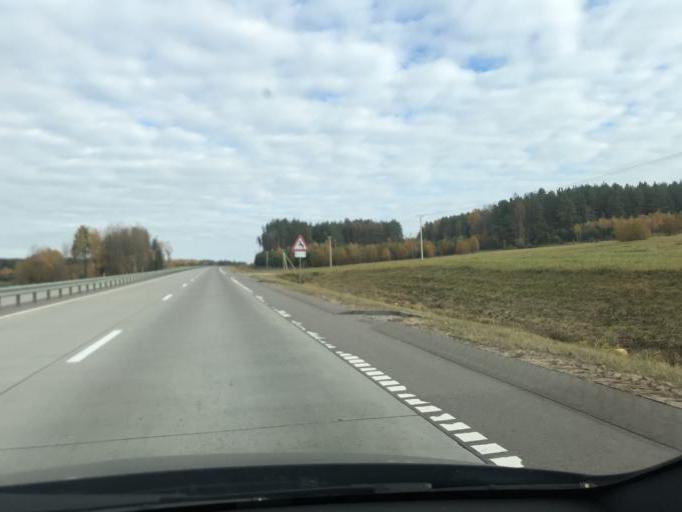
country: BY
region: Minsk
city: Rakaw
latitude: 53.9748
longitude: 27.0953
